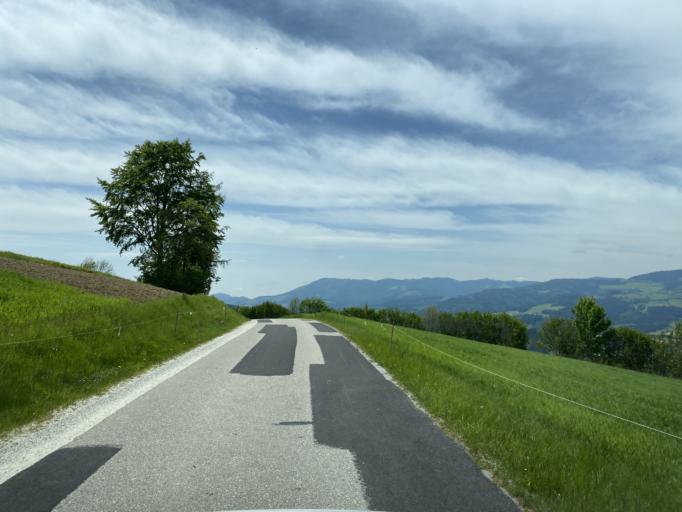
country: AT
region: Styria
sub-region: Politischer Bezirk Weiz
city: Gschaid bei Birkfeld
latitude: 47.3573
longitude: 15.7212
